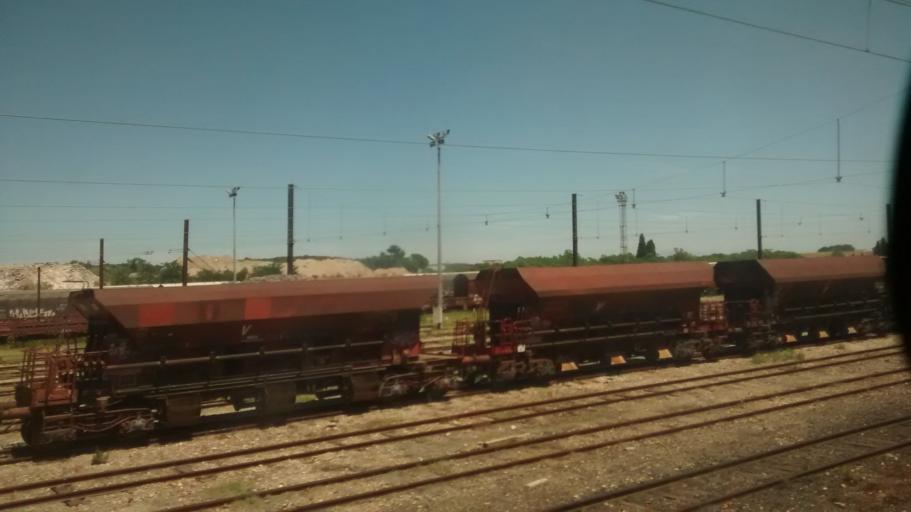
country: FR
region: Languedoc-Roussillon
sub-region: Departement du Gard
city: Rodilhan
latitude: 43.8473
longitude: 4.4046
